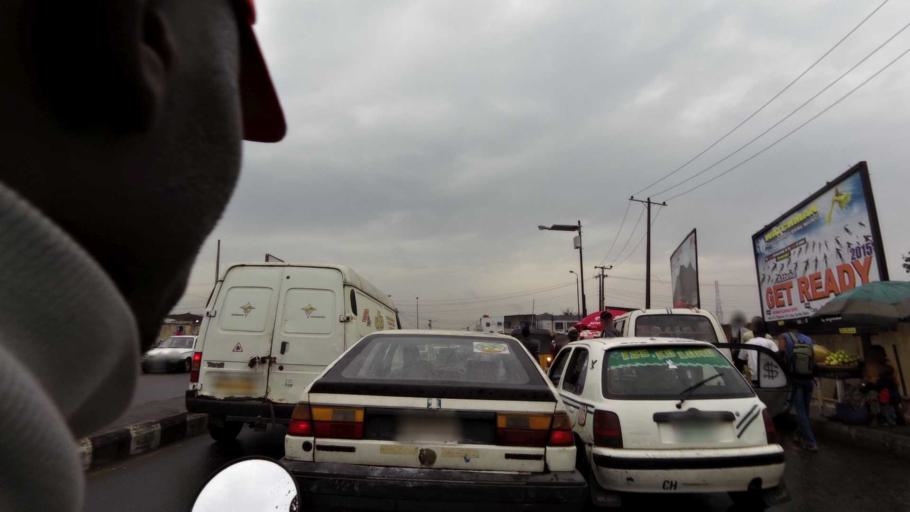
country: NG
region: Oyo
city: Ibadan
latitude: 7.3959
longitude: 3.9185
